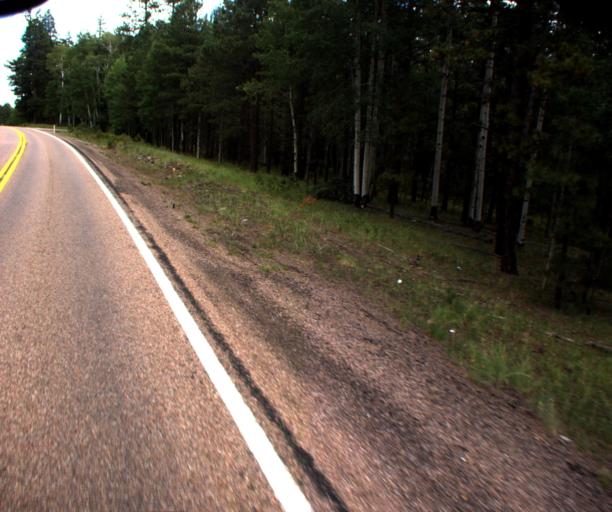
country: US
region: Arizona
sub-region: Apache County
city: Eagar
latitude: 34.0296
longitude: -109.6266
